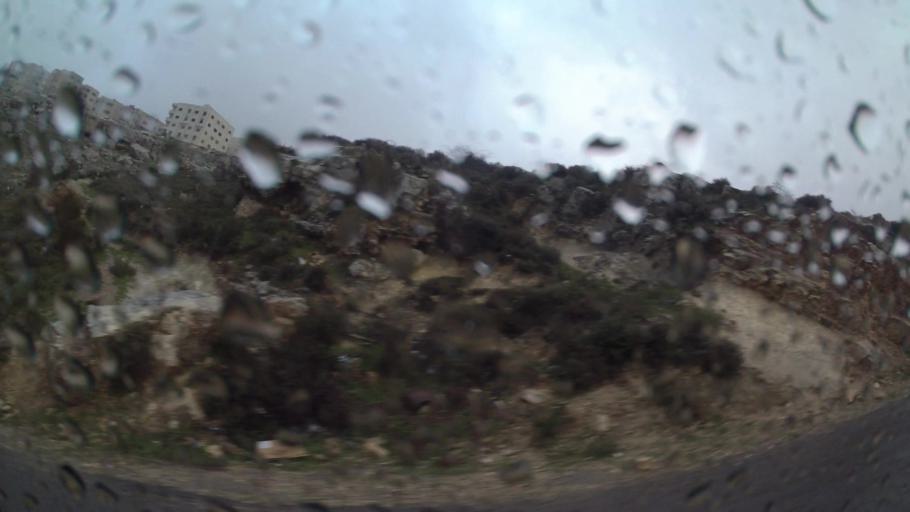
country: JO
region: Amman
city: Al Jubayhah
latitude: 32.0285
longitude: 35.8427
